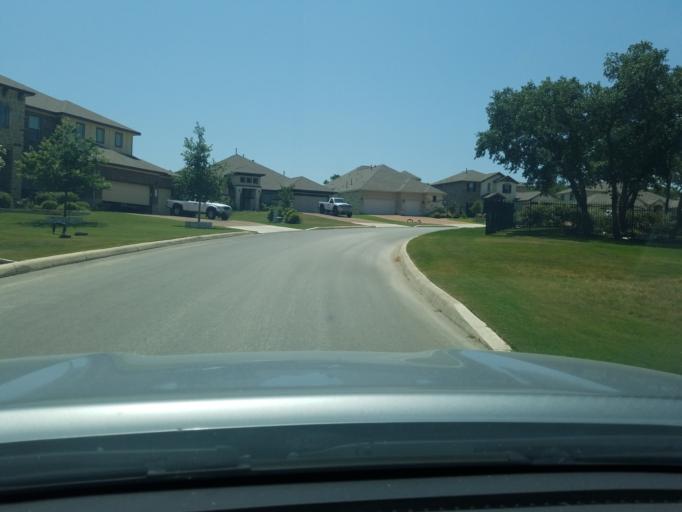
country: US
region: Texas
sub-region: Bexar County
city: Timberwood Park
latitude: 29.7113
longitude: -98.5108
